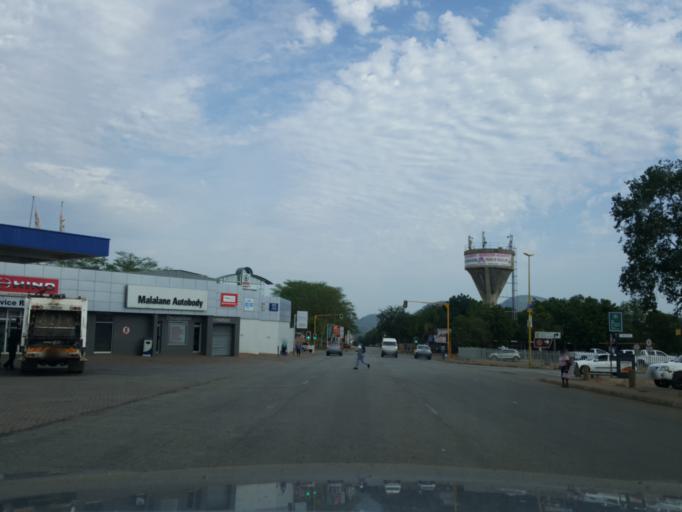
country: SZ
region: Hhohho
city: Ntfonjeni
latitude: -25.4991
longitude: 31.5089
